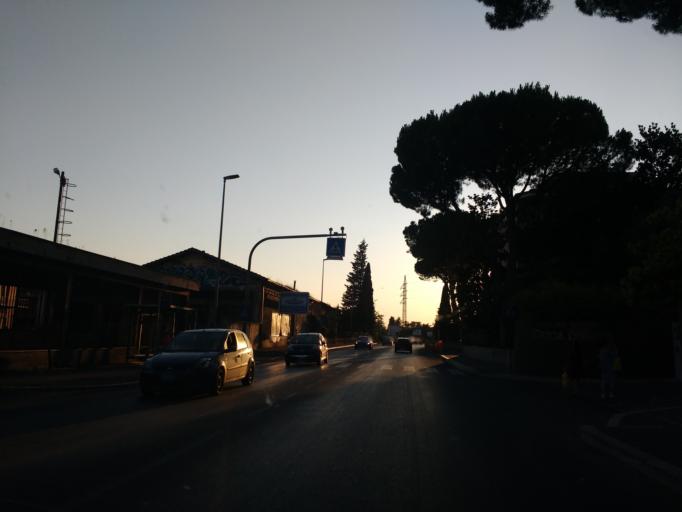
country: IT
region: Latium
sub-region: Citta metropolitana di Roma Capitale
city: Bagni di Tivoli
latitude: 41.9527
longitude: 12.7160
